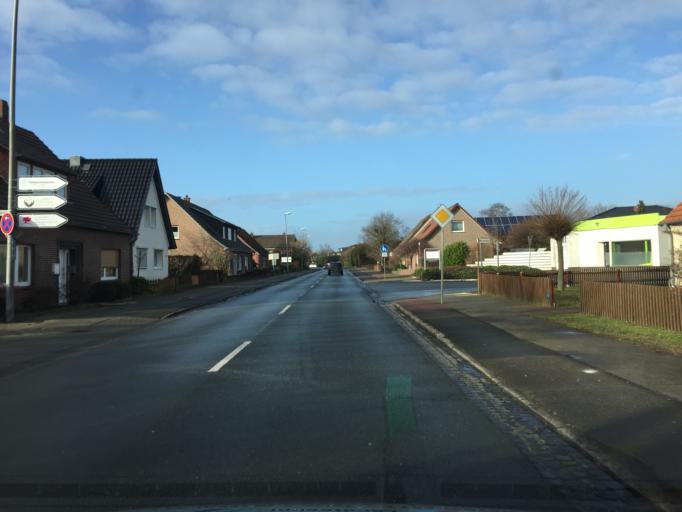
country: DE
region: Lower Saxony
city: Sulingen
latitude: 52.6848
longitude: 8.7905
